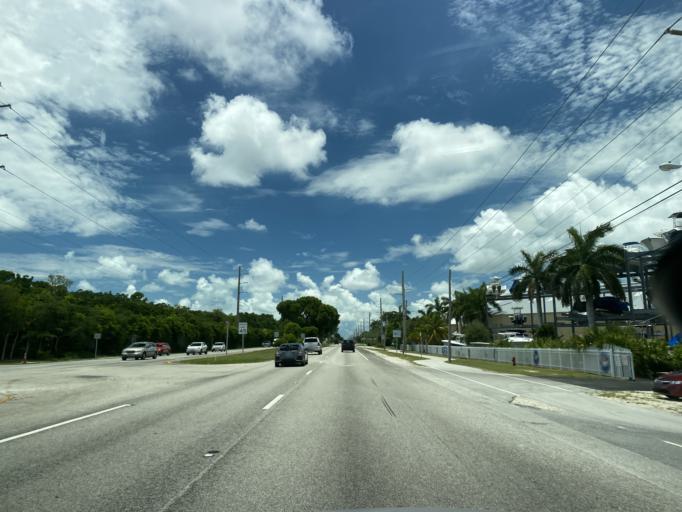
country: US
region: Florida
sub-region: Monroe County
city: Key Largo
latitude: 25.1434
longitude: -80.3977
